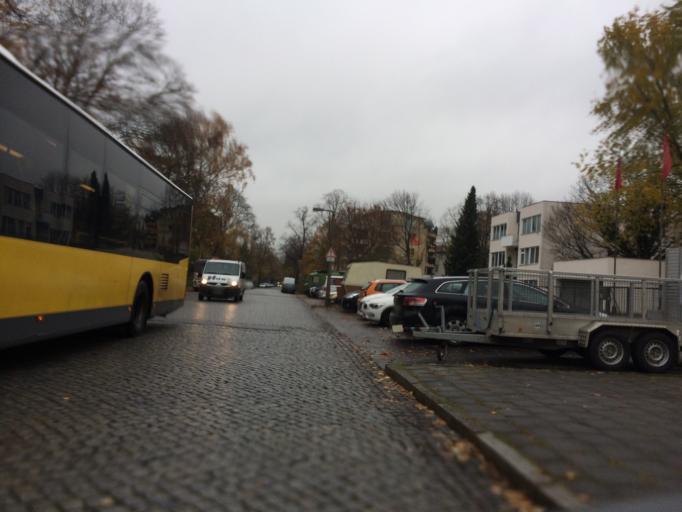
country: DE
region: Berlin
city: Niederschonhausen
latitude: 52.5834
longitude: 13.3987
